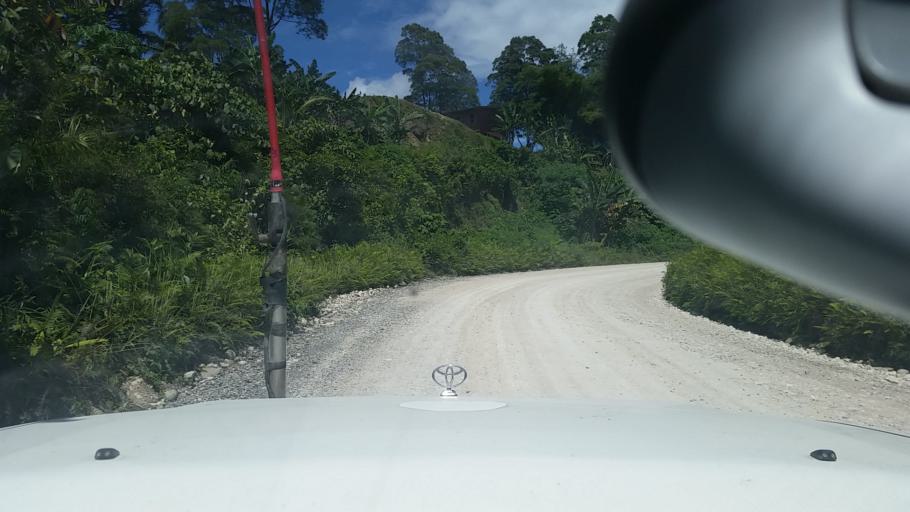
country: PG
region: Western Province
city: Kiunga
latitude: -5.5774
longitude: 141.2394
